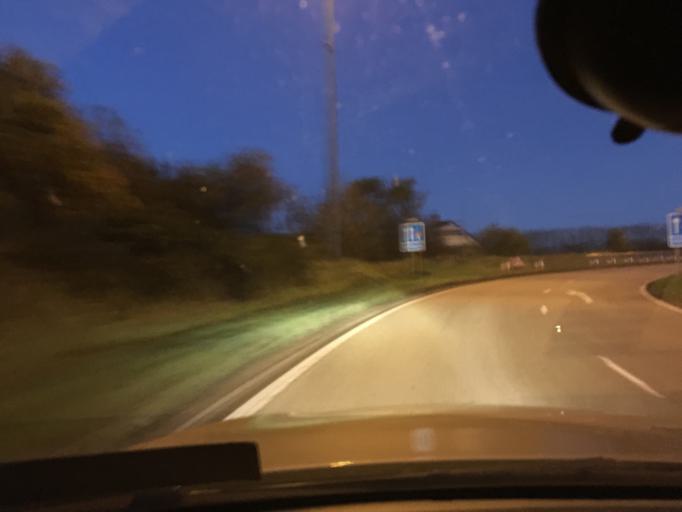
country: GB
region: Northern Ireland
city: Hillsborough
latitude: 54.4948
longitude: -6.0627
